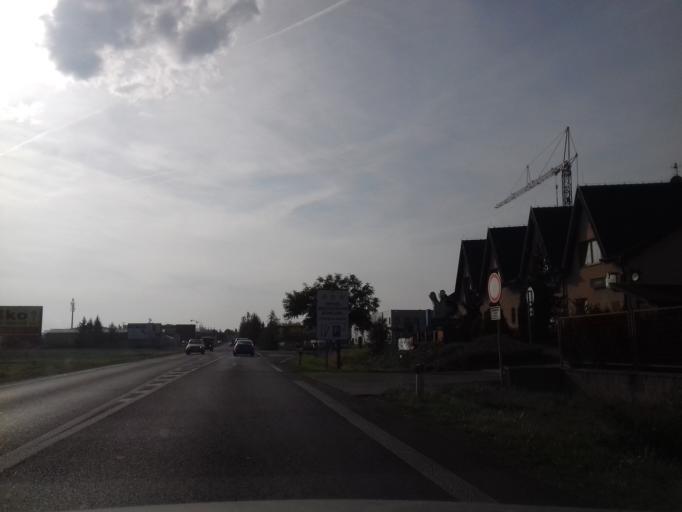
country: CZ
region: Central Bohemia
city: Vestec
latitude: 49.9906
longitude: 14.4906
